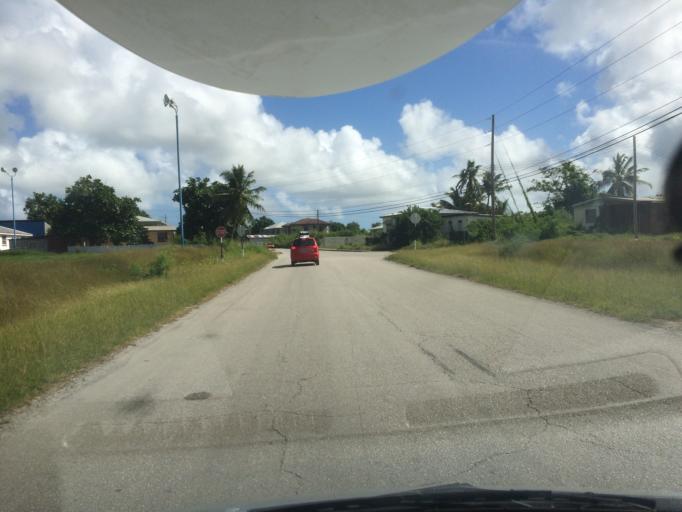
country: BB
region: Saint Lucy
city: Checker Hall
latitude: 13.2854
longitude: -59.6424
